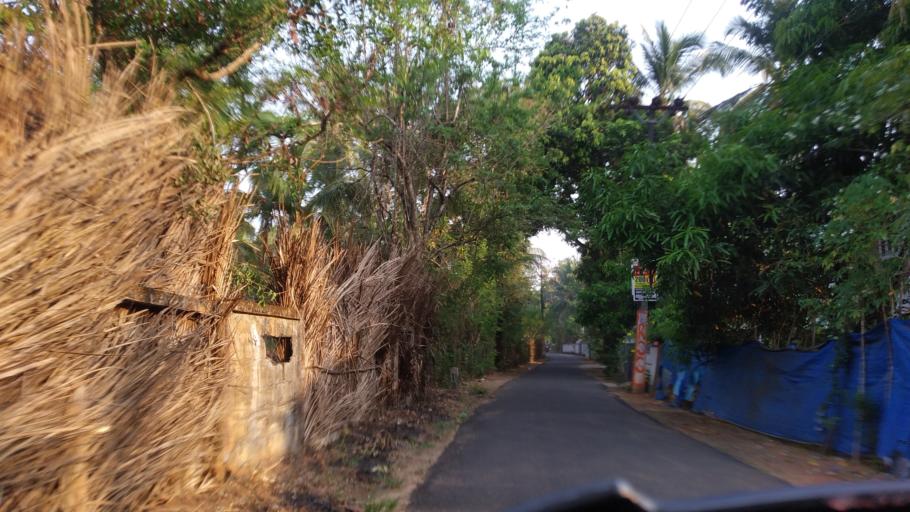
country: IN
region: Kerala
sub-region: Thrissur District
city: Thanniyam
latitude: 10.4306
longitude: 76.0797
